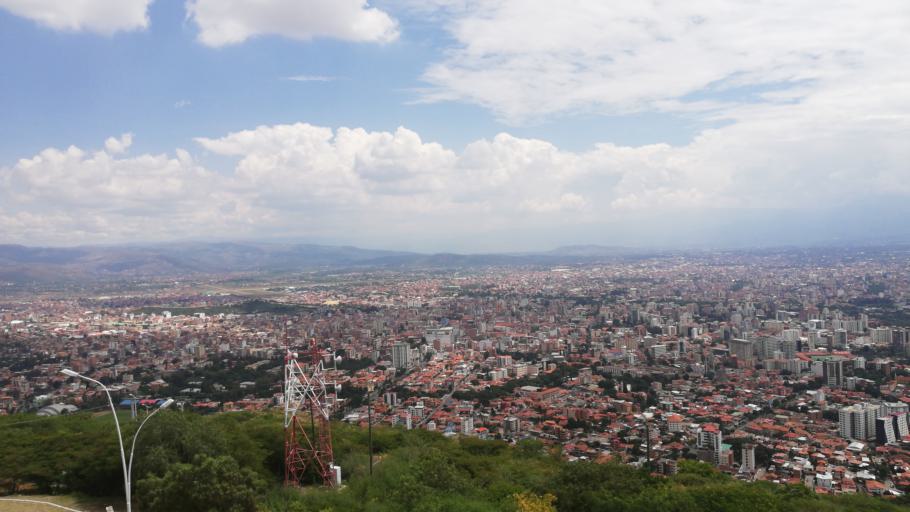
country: BO
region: Cochabamba
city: Cochabamba
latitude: -17.3841
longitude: -66.1353
